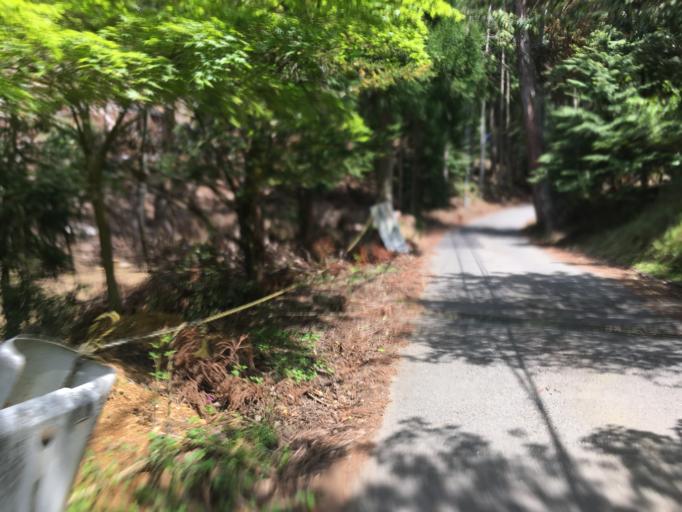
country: JP
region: Kyoto
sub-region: Kyoto-shi
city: Kamigyo-ku
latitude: 35.0742
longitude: 135.7174
